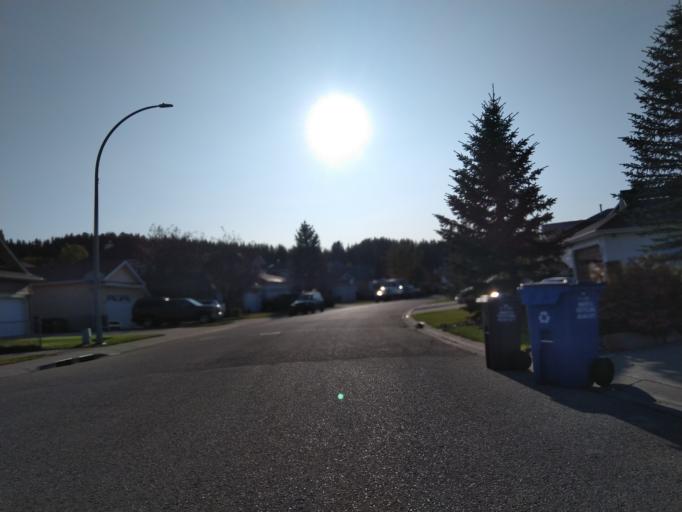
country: CA
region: Alberta
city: Cochrane
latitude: 51.1740
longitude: -114.4699
